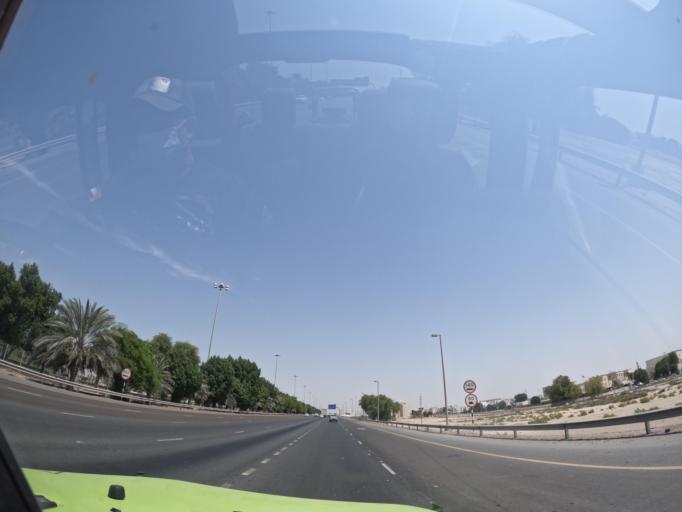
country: AE
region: Abu Dhabi
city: Abu Dhabi
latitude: 24.3225
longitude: 54.6166
